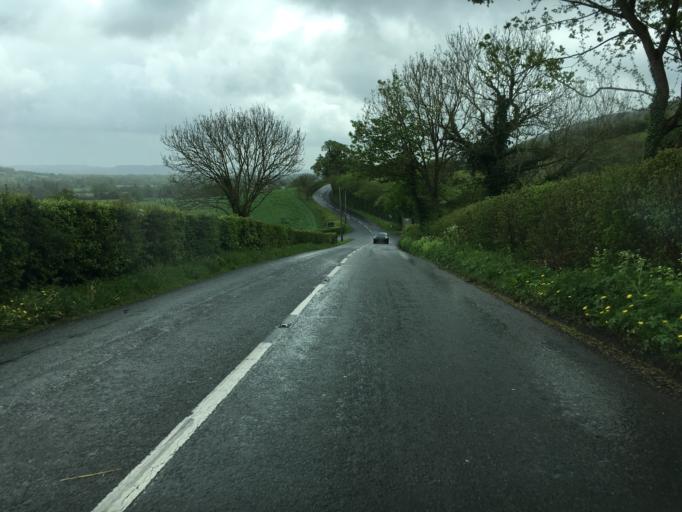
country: GB
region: England
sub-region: North Somerset
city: Blagdon
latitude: 51.3236
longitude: -2.6986
